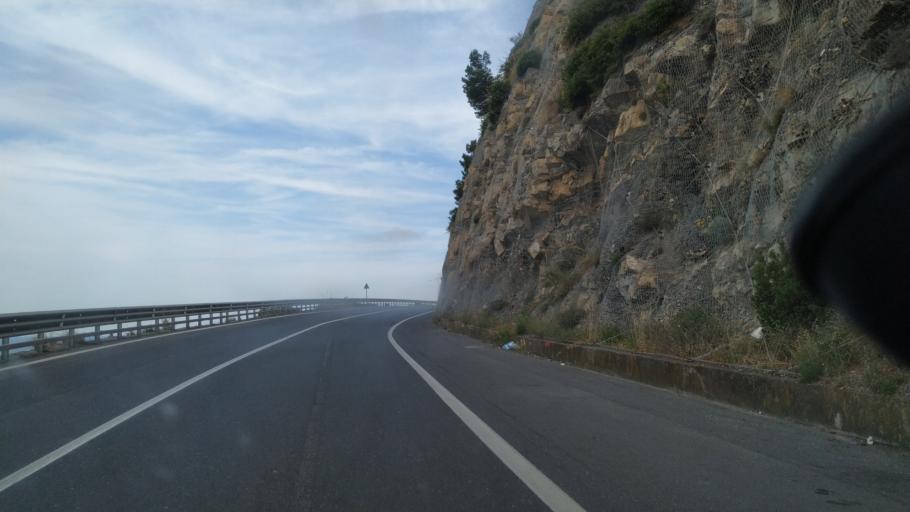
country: IT
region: Liguria
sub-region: Provincia di Savona
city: Marina di Andora
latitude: 43.9622
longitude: 8.1679
